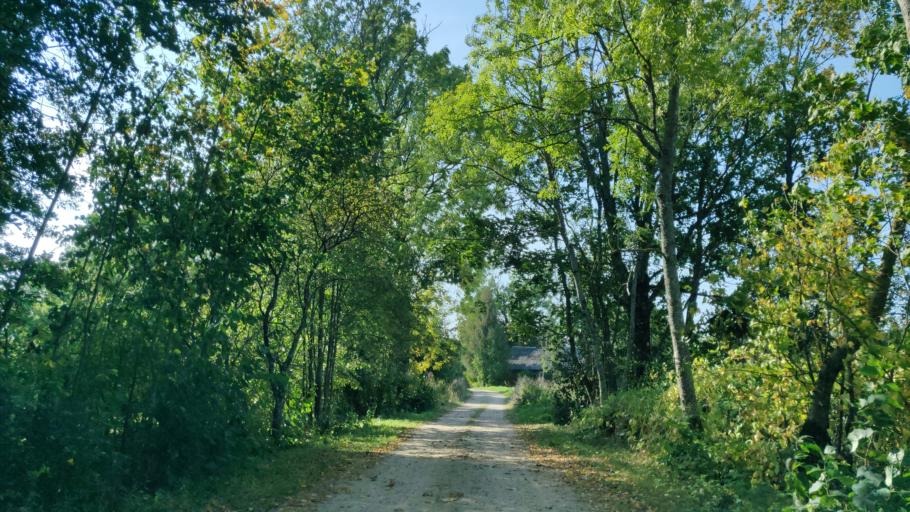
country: LT
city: Sirvintos
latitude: 54.9620
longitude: 24.7845
